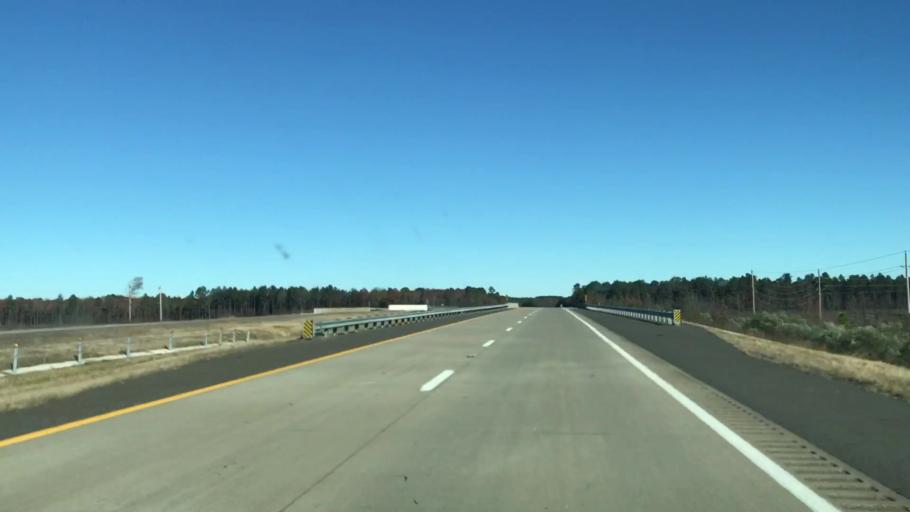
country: US
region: Texas
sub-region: Bowie County
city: Texarkana
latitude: 33.2234
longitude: -93.8733
